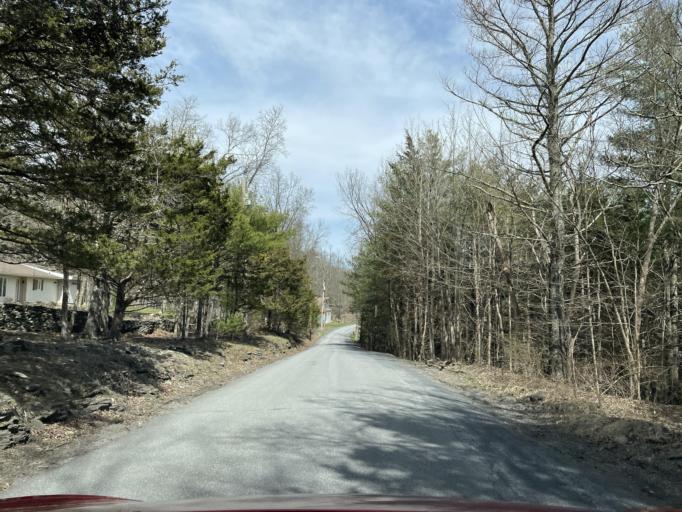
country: US
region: New York
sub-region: Ulster County
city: Zena
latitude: 42.0418
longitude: -74.0866
